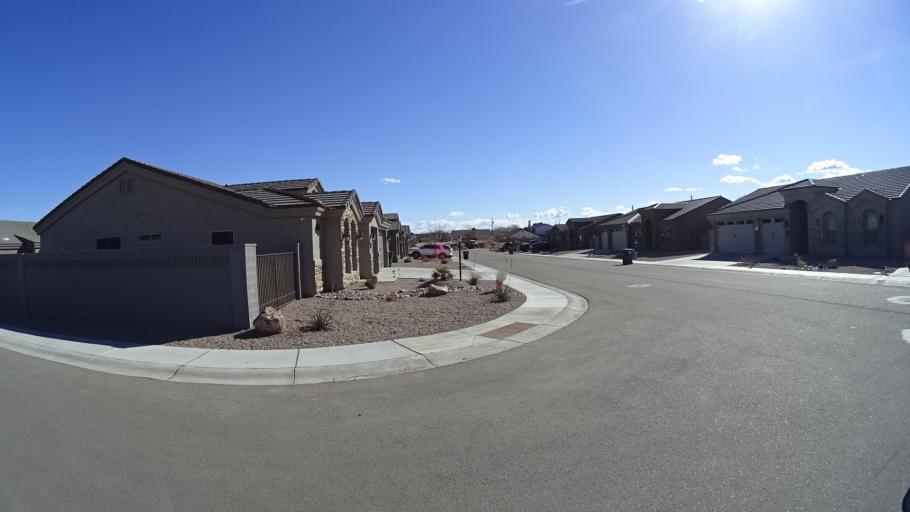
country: US
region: Arizona
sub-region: Mohave County
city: New Kingman-Butler
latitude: 35.2330
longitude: -114.0220
